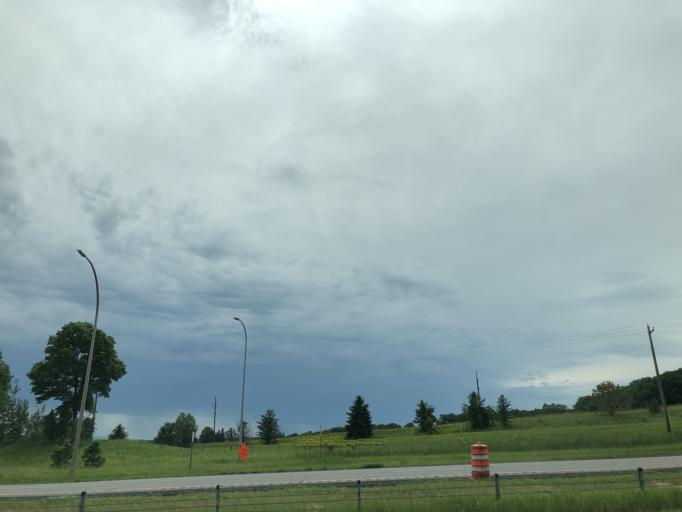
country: US
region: Minnesota
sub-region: Stearns County
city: Collegeville
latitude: 45.6031
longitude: -94.3935
